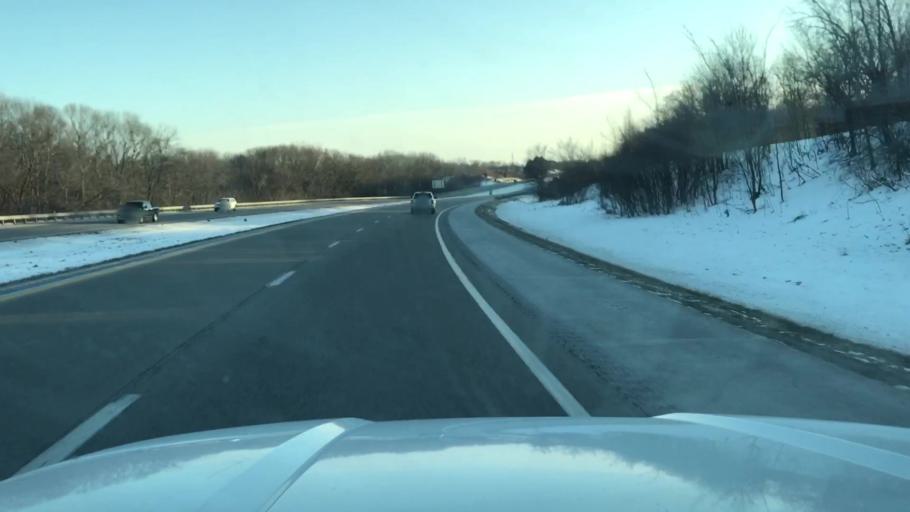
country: US
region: Missouri
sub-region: Andrew County
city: Country Club Village
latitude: 39.8529
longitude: -94.8058
